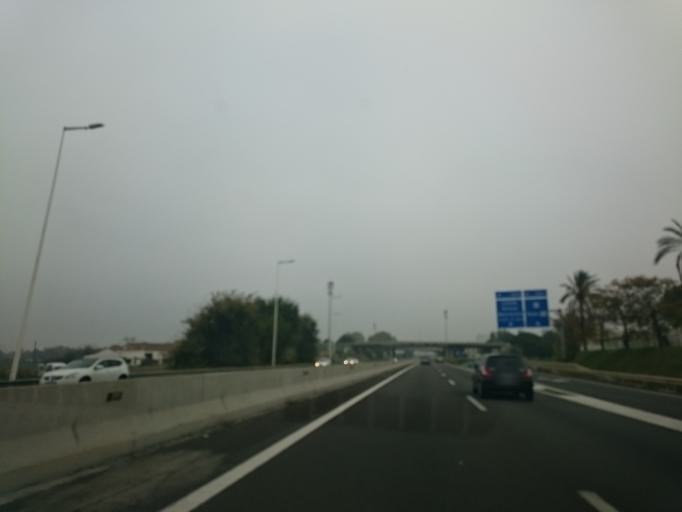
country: ES
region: Catalonia
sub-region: Provincia de Barcelona
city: El Prat de Llobregat
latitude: 41.3191
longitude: 2.0727
